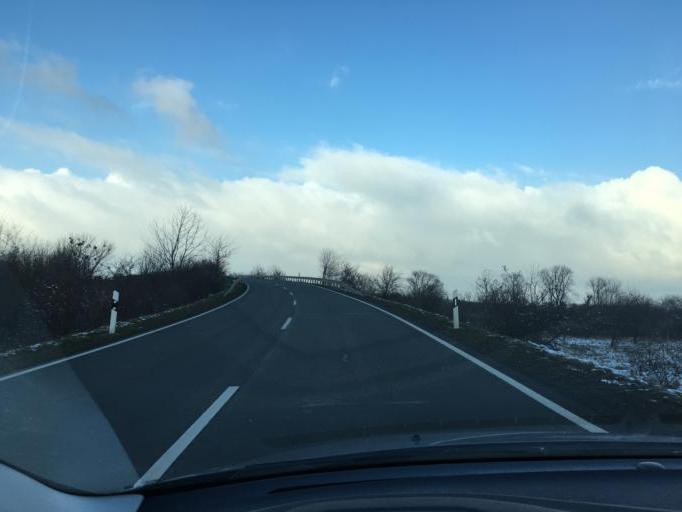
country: DE
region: Saxony
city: Brandis
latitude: 51.3544
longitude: 12.5979
